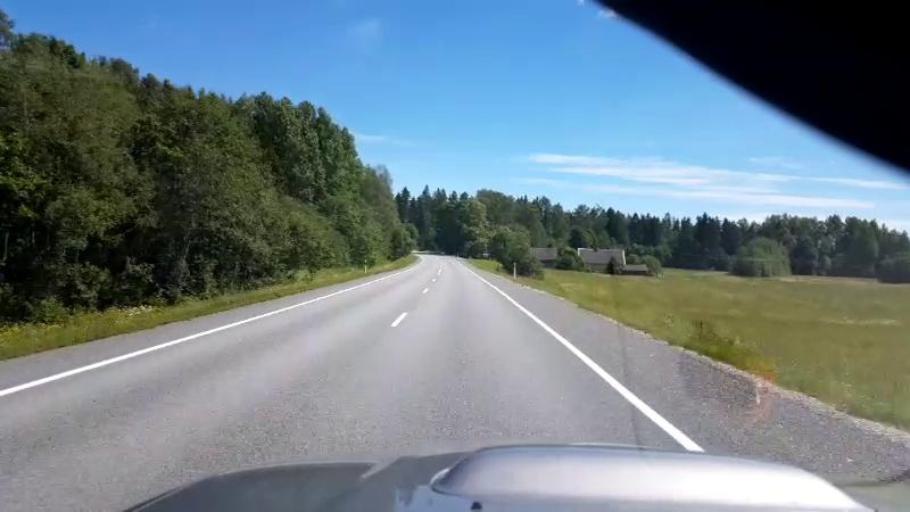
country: EE
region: Jaervamaa
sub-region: Jaerva-Jaani vald
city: Jarva-Jaani
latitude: 58.9980
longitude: 25.9418
